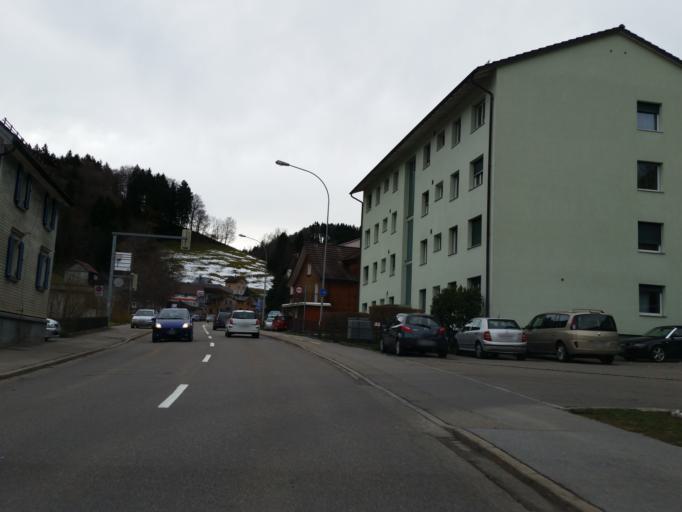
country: CH
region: Appenzell Ausserrhoden
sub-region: Bezirk Hinterland
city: Waldstatt
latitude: 47.3710
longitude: 9.2820
